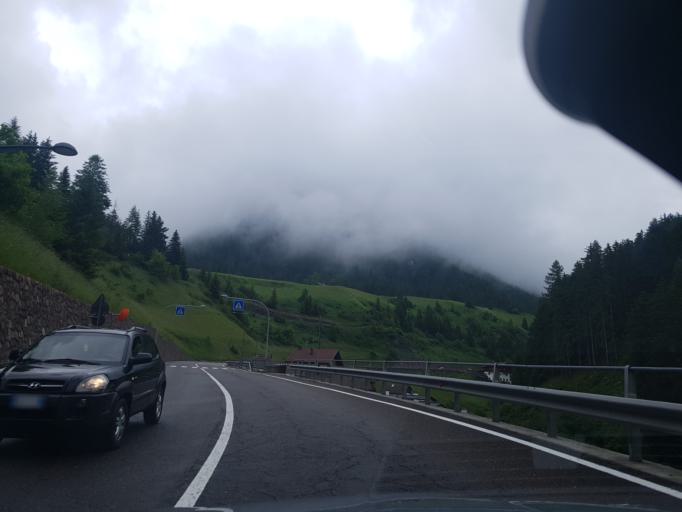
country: IT
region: Trentino-Alto Adige
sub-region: Bolzano
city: Santa Cristina Valgardena
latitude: 46.5580
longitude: 11.7329
